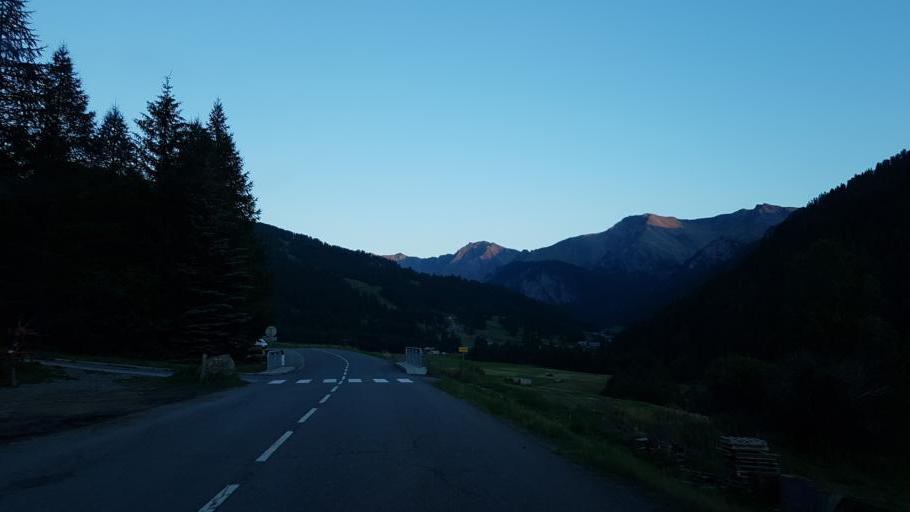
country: FR
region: Provence-Alpes-Cote d'Azur
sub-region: Departement des Hautes-Alpes
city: Guillestre
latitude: 44.7299
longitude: 6.8423
